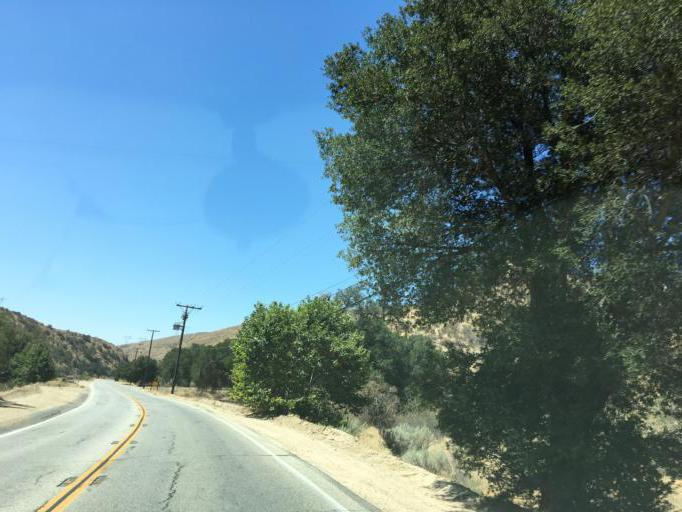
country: US
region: California
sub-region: Los Angeles County
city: Agua Dulce
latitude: 34.5014
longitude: -118.3811
